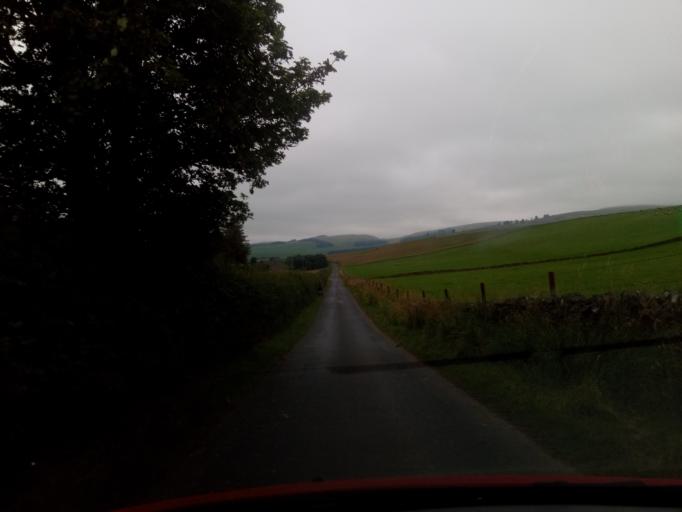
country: GB
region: Scotland
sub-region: The Scottish Borders
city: Galashiels
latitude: 55.6885
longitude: -2.8695
